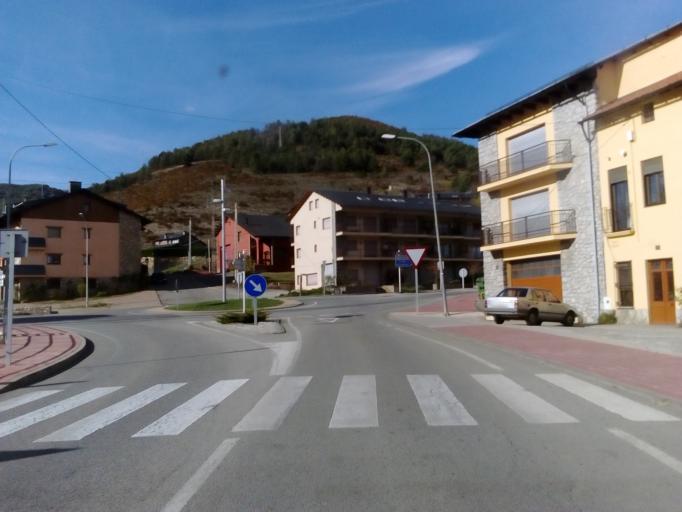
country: ES
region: Catalonia
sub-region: Provincia de Lleida
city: Bellver de Cerdanya
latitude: 42.3724
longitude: 1.7751
